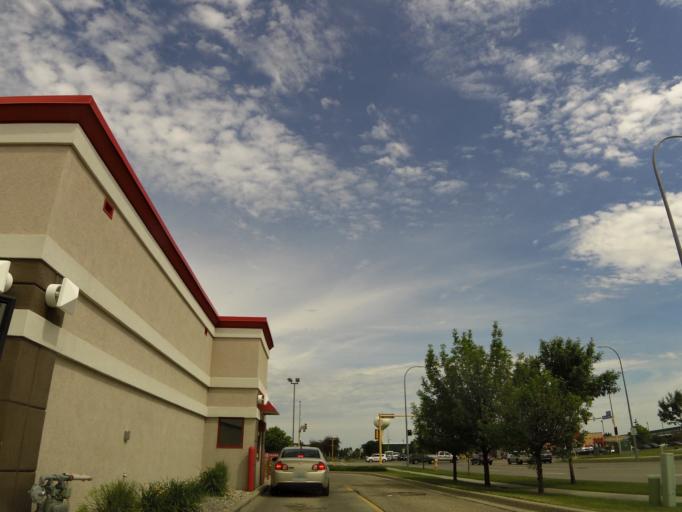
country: US
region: North Dakota
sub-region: Grand Forks County
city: Grand Forks
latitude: 47.8886
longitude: -97.0833
